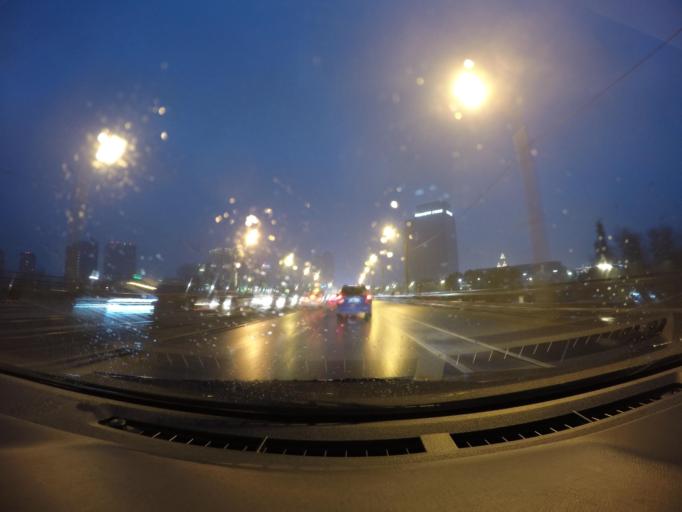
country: RU
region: Moskovskaya
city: Kozhukhovo
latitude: 55.6882
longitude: 37.6656
